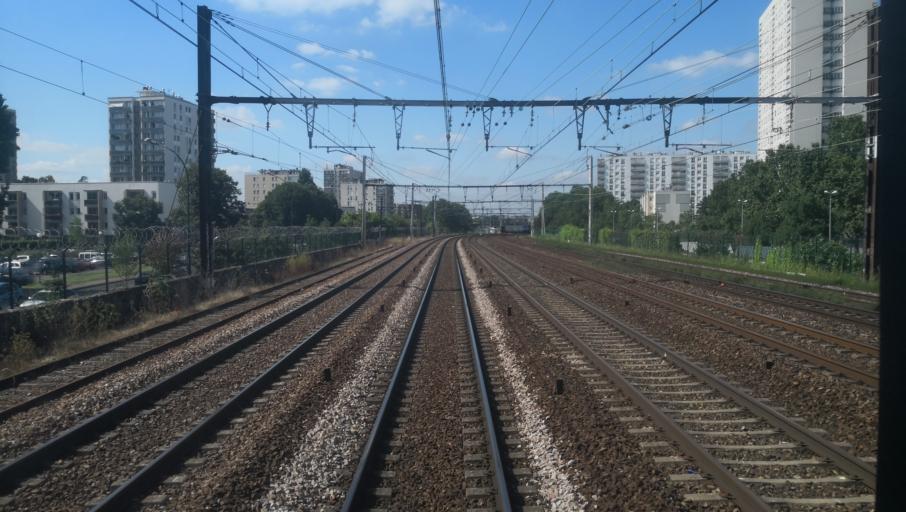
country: FR
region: Ile-de-France
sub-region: Departement du Val-de-Marne
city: Alfortville
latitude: 48.7917
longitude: 2.4307
